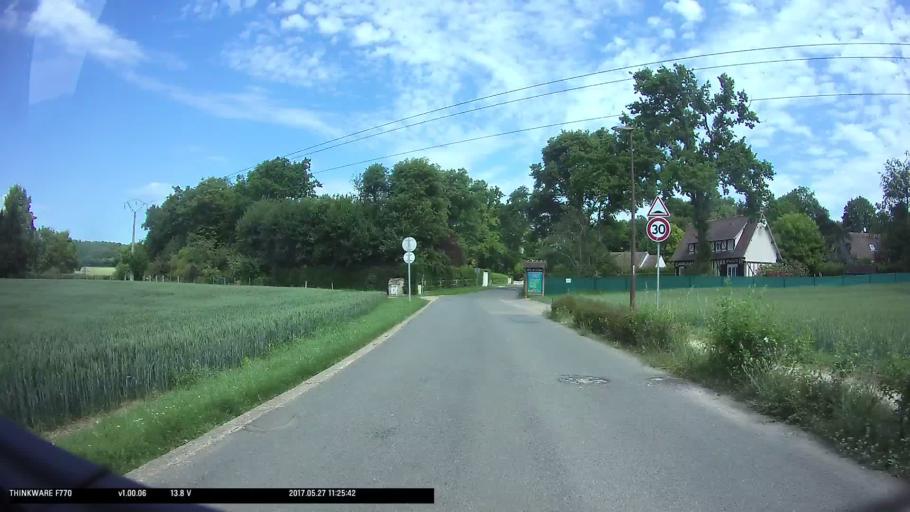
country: FR
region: Picardie
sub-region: Departement de l'Oise
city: Trie-Chateau
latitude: 49.2905
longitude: 1.8187
